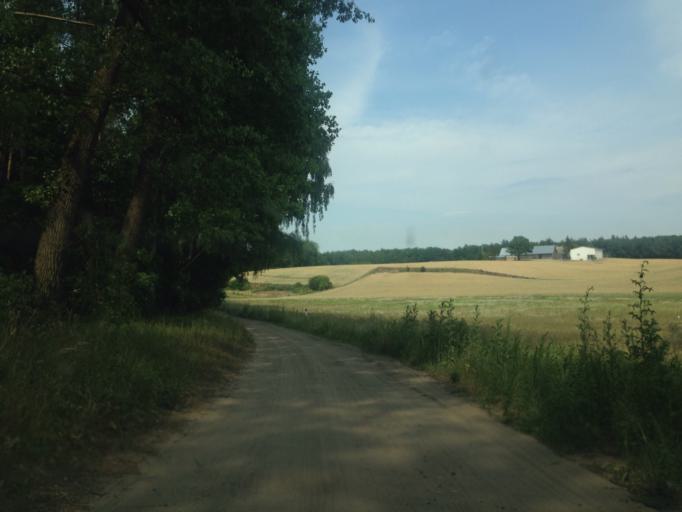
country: PL
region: Kujawsko-Pomorskie
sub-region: Powiat brodnicki
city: Bobrowo
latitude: 53.2597
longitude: 19.2993
